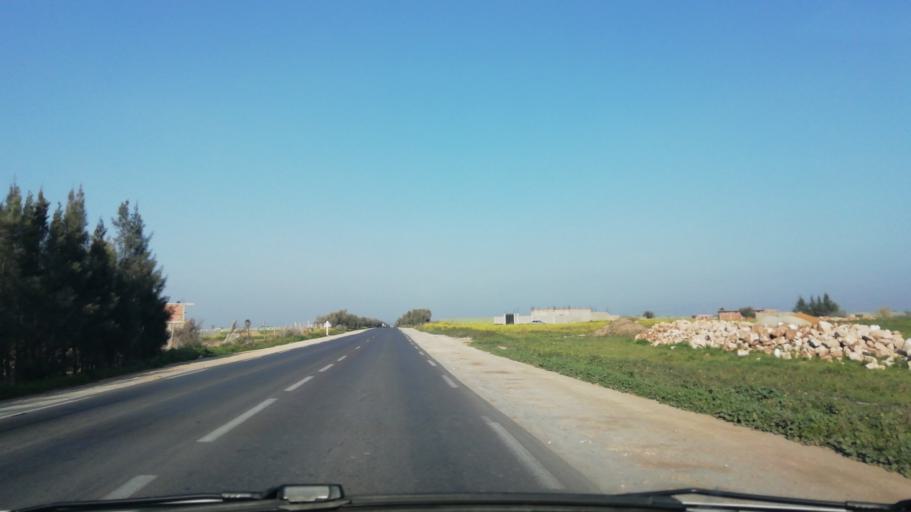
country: DZ
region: Mostaganem
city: Mostaganem
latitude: 35.7448
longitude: 0.1441
